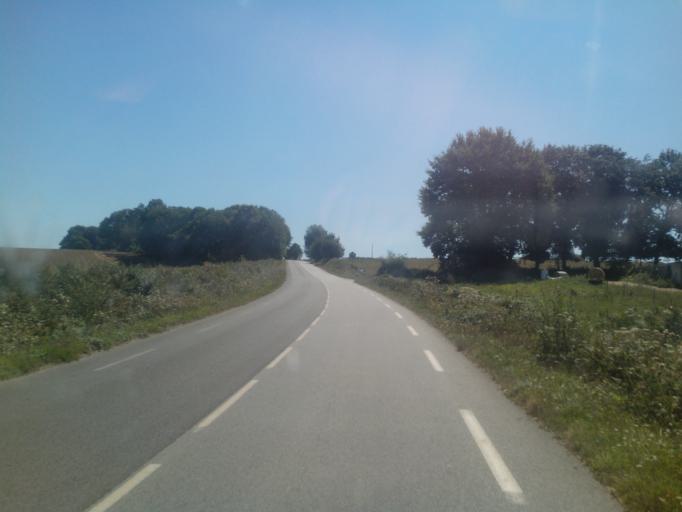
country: FR
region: Brittany
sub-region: Departement du Morbihan
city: Josselin
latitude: 47.9261
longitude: -2.5306
